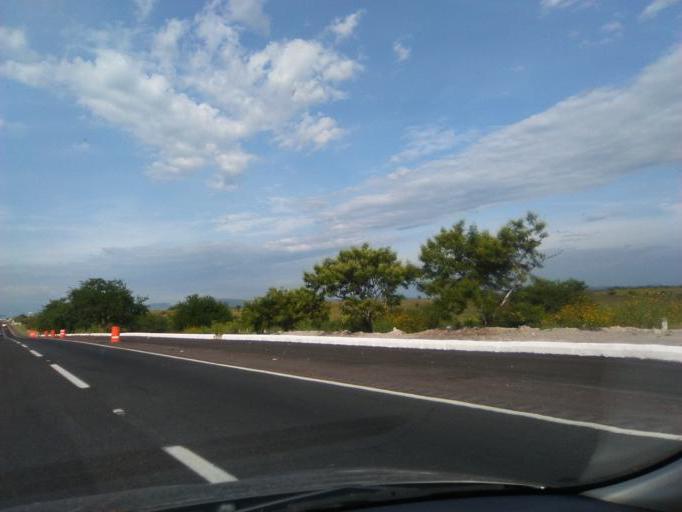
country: MX
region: Morelos
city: Ahuehuetzingo
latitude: 18.6861
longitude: -99.2861
